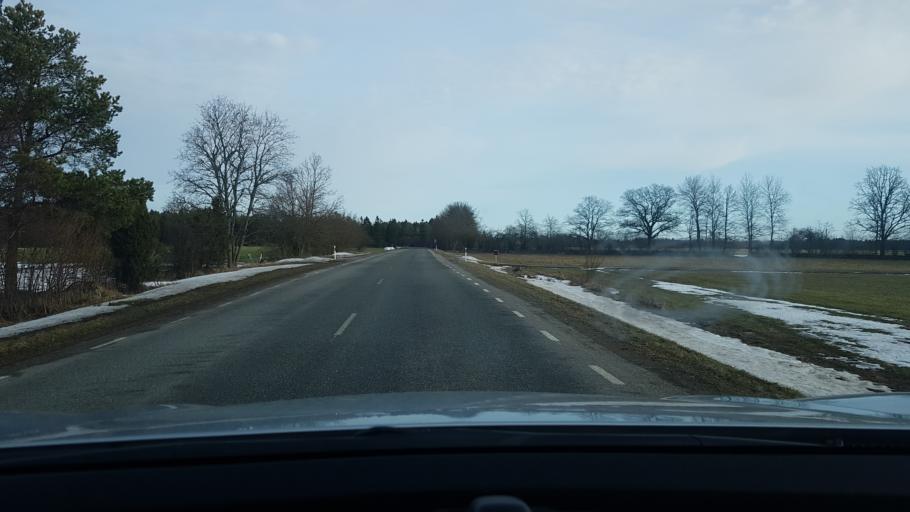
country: EE
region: Saare
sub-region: Kuressaare linn
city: Kuressaare
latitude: 58.4068
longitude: 22.6499
